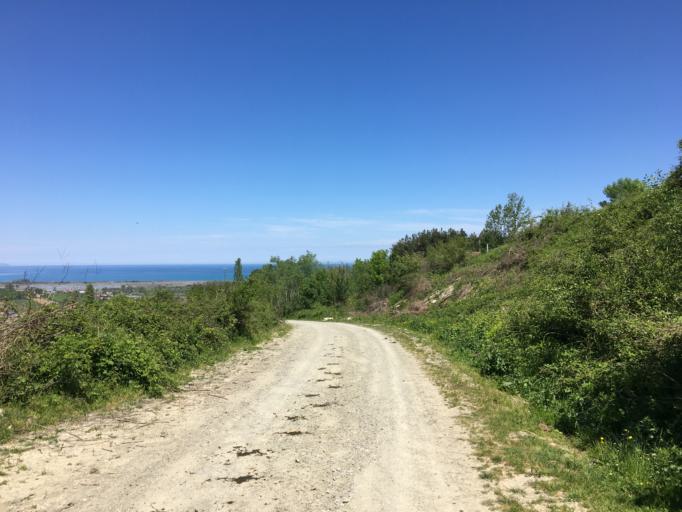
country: TR
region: Samsun
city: Alacam
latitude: 41.6031
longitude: 35.6066
